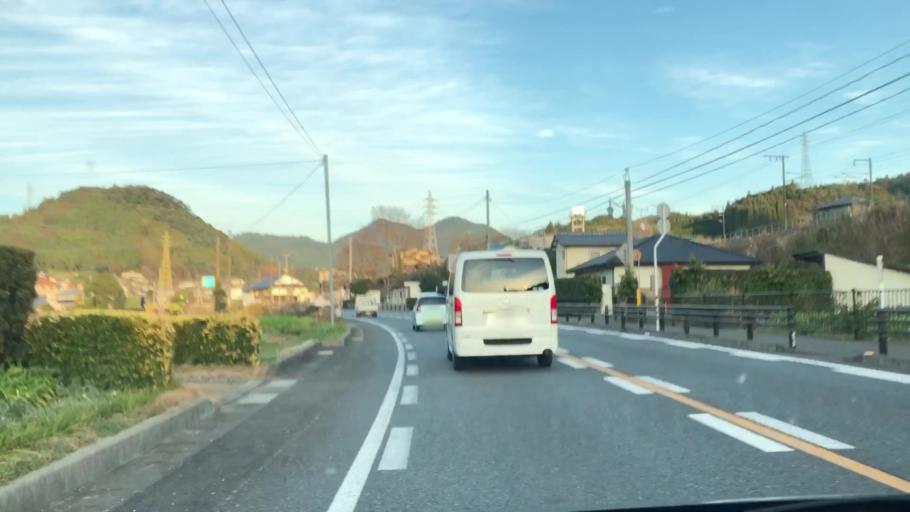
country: JP
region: Kumamoto
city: Minamata
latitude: 32.2313
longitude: 130.4607
